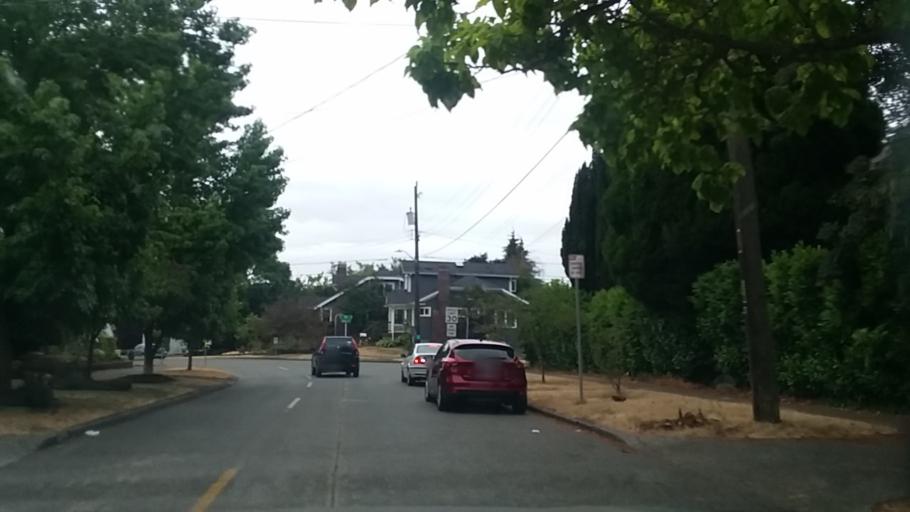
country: US
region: Washington
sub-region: King County
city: Shoreline
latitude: 47.6845
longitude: -122.3472
